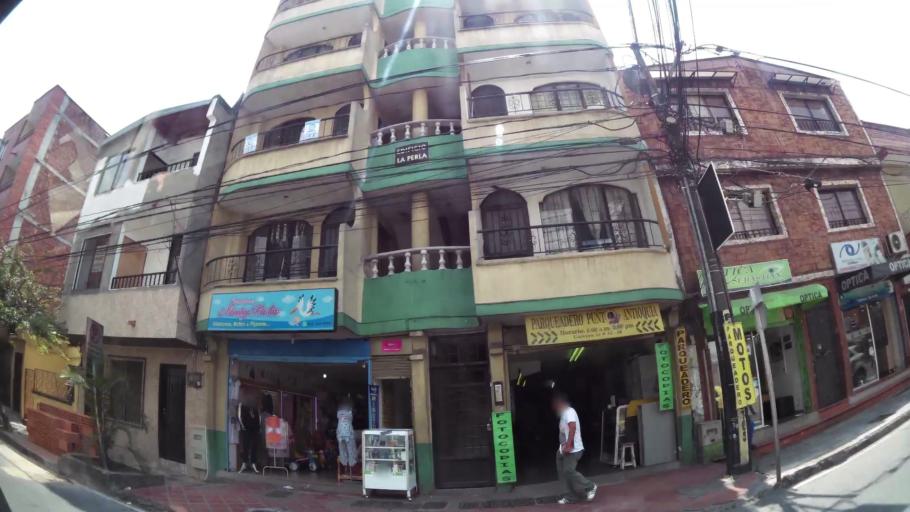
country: CO
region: Antioquia
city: Sabaneta
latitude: 6.1695
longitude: -75.6126
